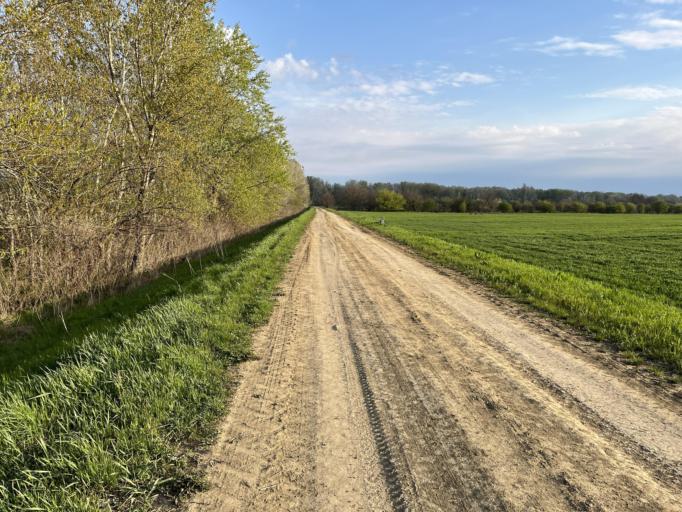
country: HU
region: Jasz-Nagykun-Szolnok
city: Szajol
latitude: 47.1783
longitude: 20.2850
